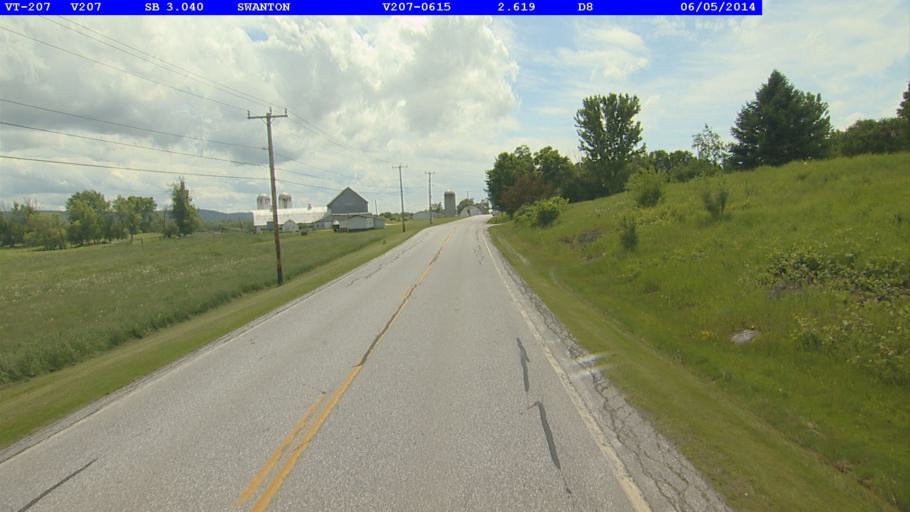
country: US
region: Vermont
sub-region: Franklin County
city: Swanton
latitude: 44.8820
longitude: -73.0688
